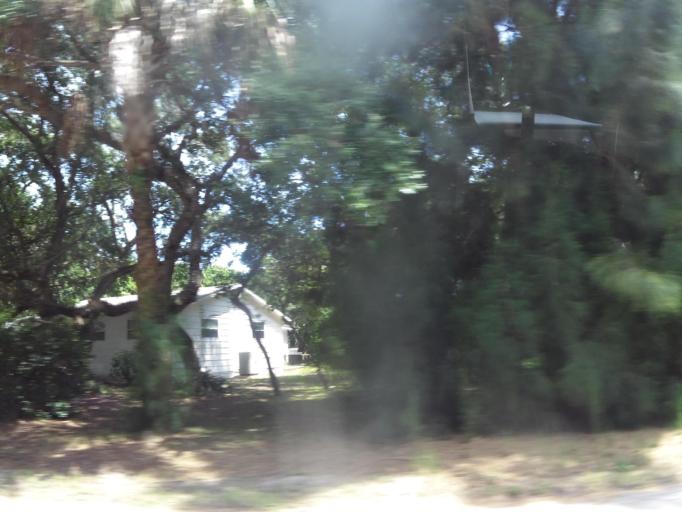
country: US
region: Florida
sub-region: Volusia County
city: Ponce Inlet
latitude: 29.0866
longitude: -80.9335
